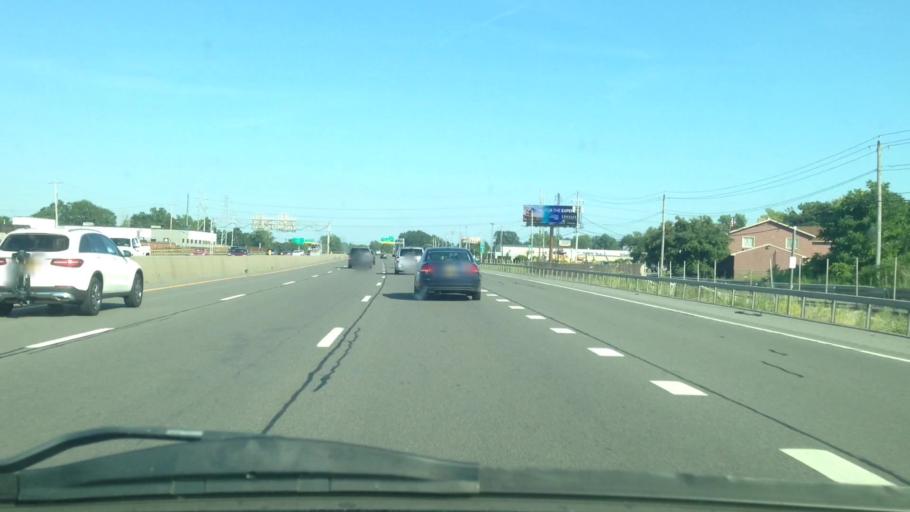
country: US
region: New York
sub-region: Onondaga County
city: Lakeland
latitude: 43.1093
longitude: -76.2606
